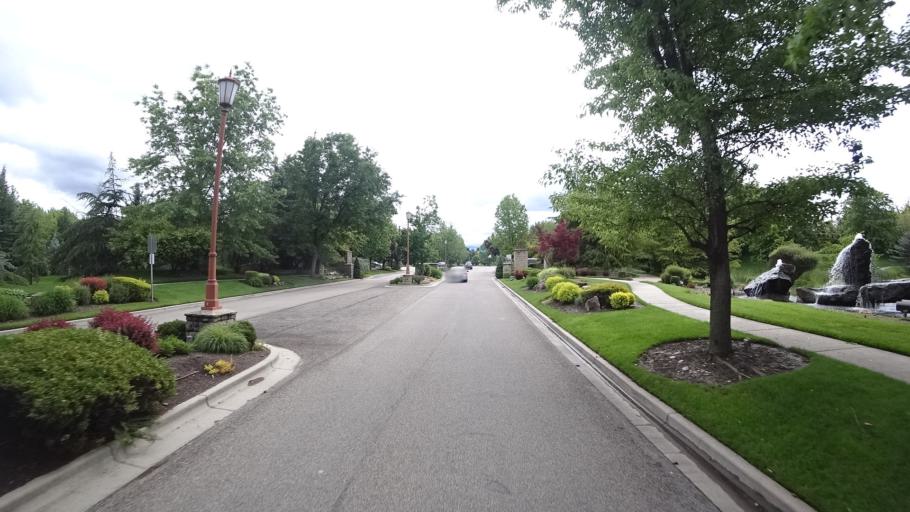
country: US
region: Idaho
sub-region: Ada County
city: Eagle
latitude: 43.6824
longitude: -116.3554
